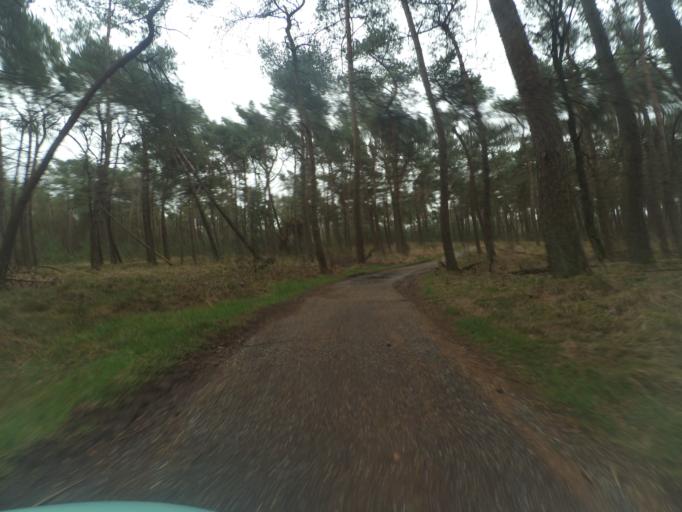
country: NL
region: Gelderland
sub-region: Gemeente Arnhem
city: Gulden Bodem
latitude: 52.0250
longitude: 5.9106
